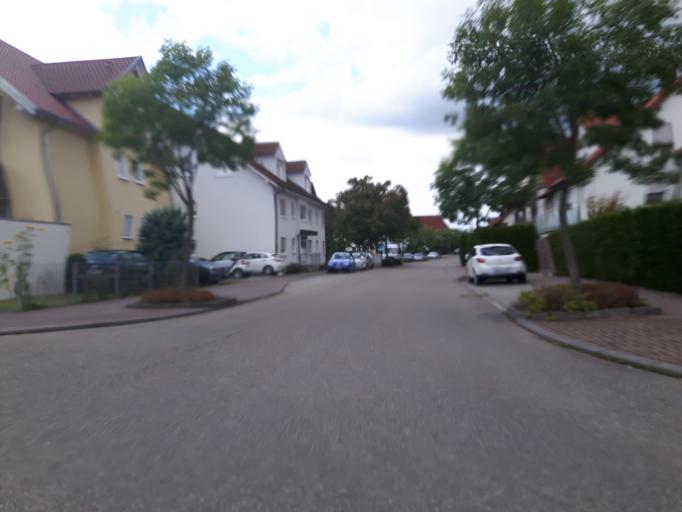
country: DE
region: Baden-Wuerttemberg
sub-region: Regierungsbezirk Stuttgart
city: Bad Wimpfen
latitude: 49.2243
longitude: 9.1514
